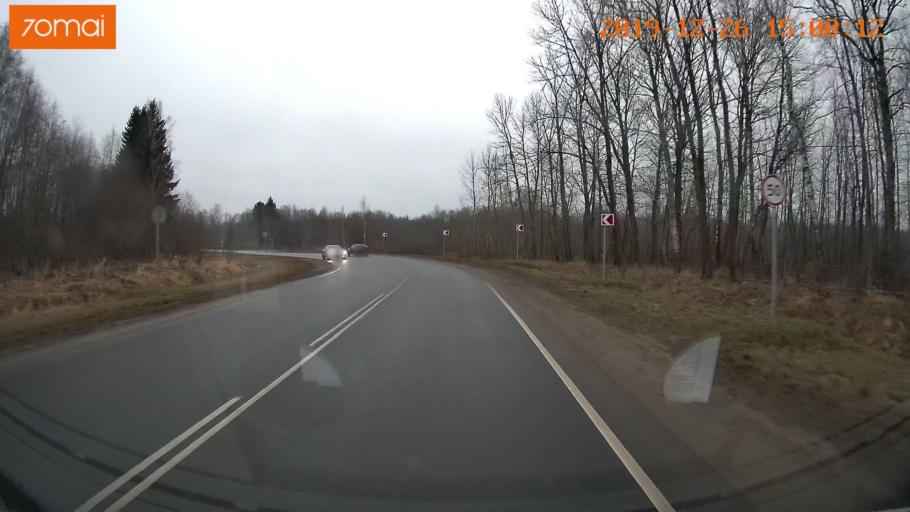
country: RU
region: Jaroslavl
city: Rybinsk
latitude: 58.2485
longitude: 38.8494
